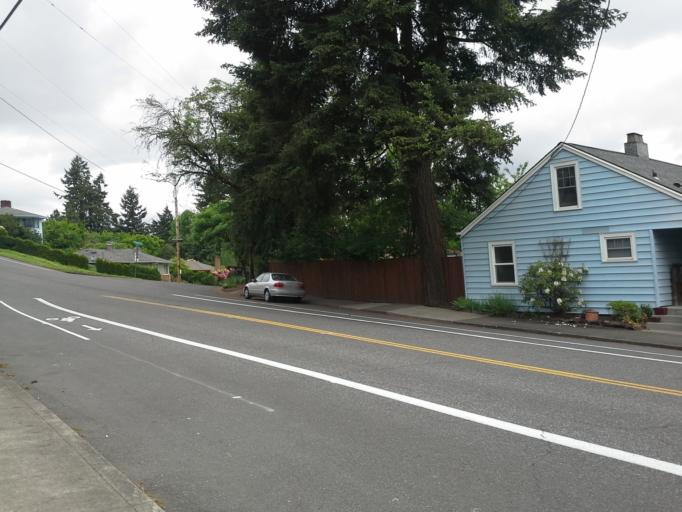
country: US
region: Oregon
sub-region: Multnomah County
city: Lents
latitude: 45.5231
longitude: -122.5920
